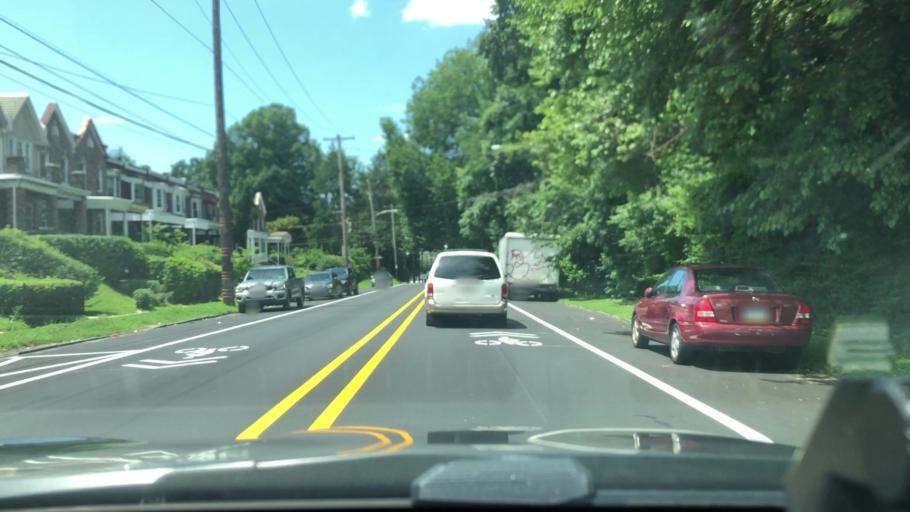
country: US
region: Pennsylvania
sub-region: Montgomery County
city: Wyndmoor
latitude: 40.0473
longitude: -75.1678
